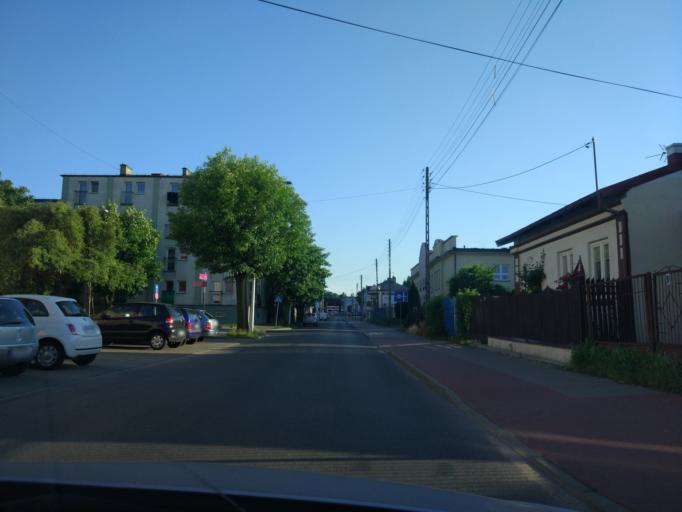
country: PL
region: Lodz Voivodeship
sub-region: Powiat kutnowski
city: Kutno
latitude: 52.2295
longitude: 19.3499
